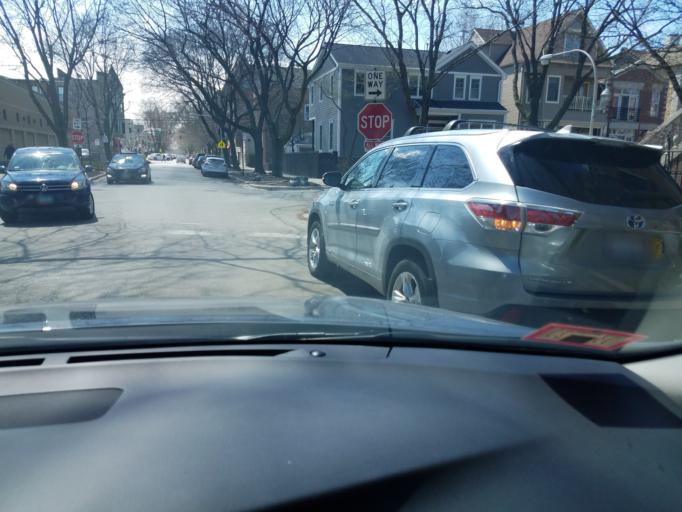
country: US
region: Illinois
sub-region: Cook County
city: Lincolnwood
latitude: 41.9409
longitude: -87.6711
